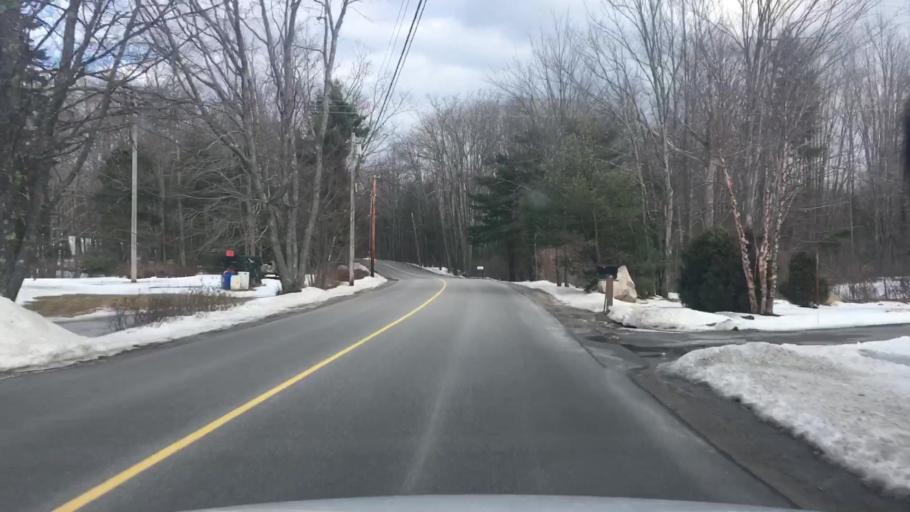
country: US
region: Maine
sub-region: York County
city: Arundel
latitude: 43.4068
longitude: -70.4863
